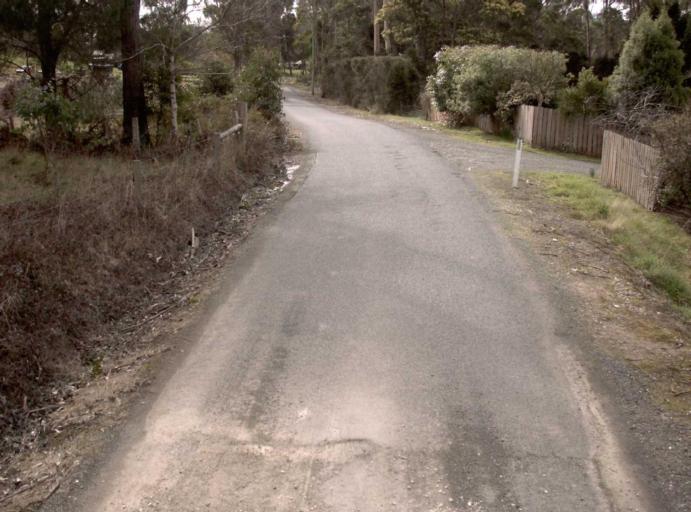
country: AU
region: Tasmania
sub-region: Launceston
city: Mayfield
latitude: -41.2704
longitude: 147.1615
